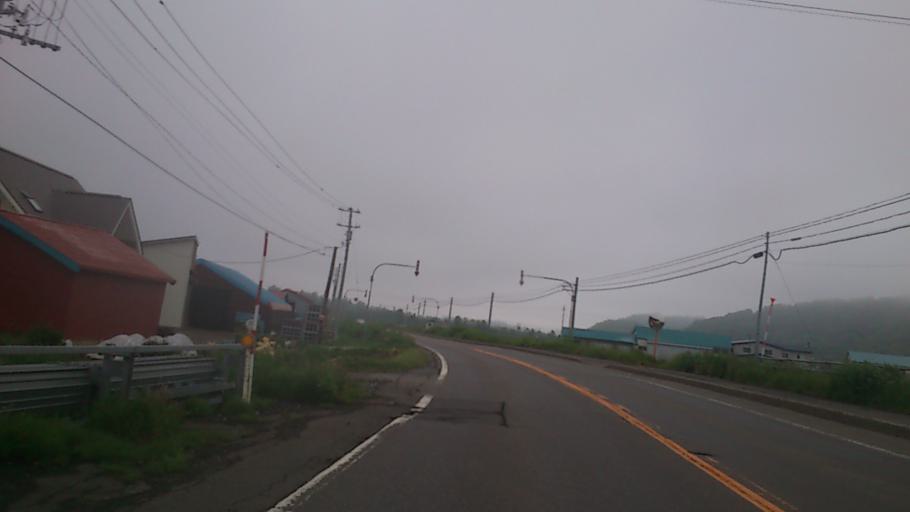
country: JP
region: Hokkaido
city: Niseko Town
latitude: 42.8233
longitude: 140.8917
